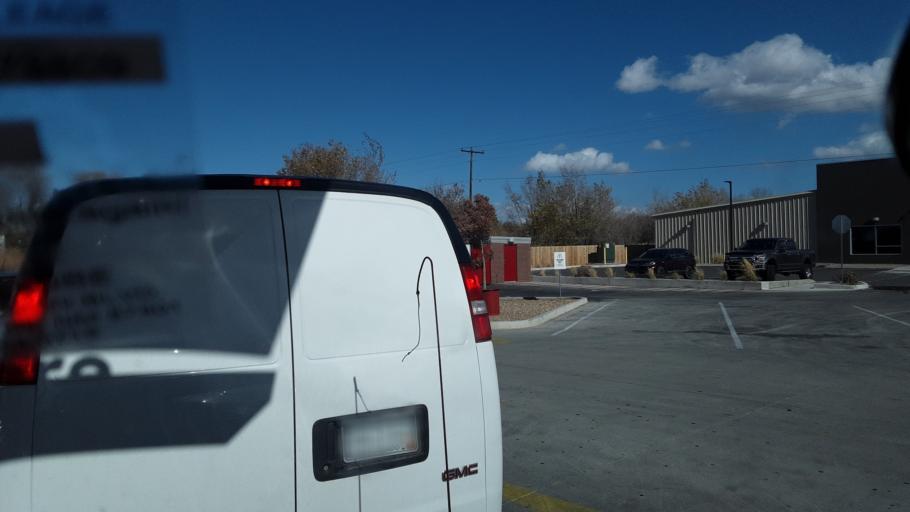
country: US
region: New Mexico
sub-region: Rio Arriba County
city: Espanola
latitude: 36.0126
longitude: -106.0637
